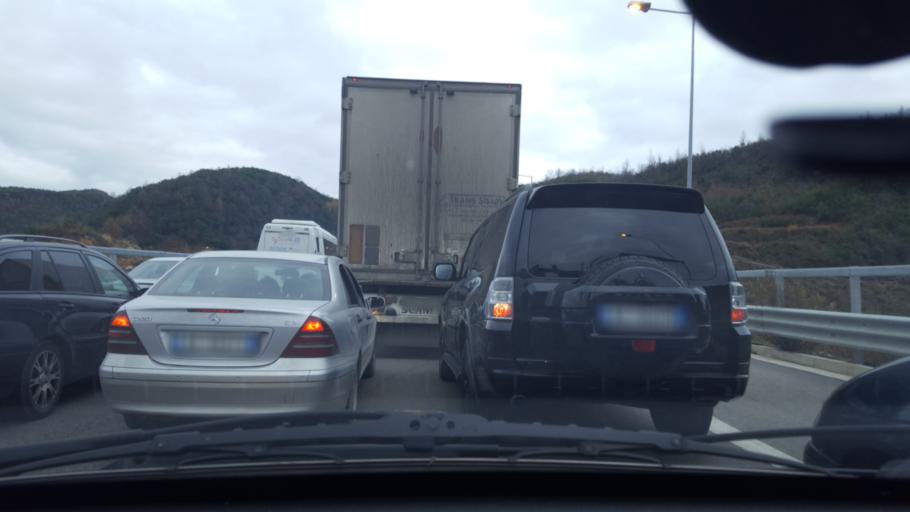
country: AL
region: Tirane
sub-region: Rrethi i Tiranes
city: Krrabe
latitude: 41.2100
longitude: 19.9577
